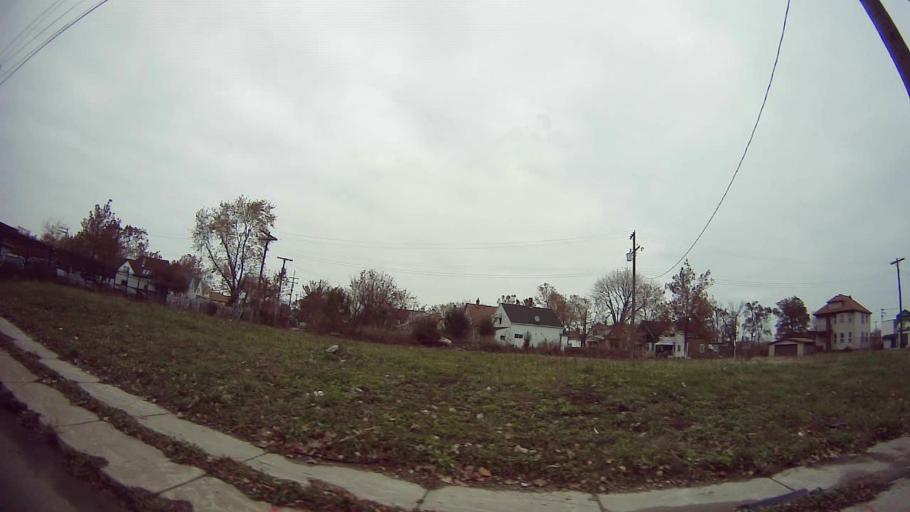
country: US
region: Michigan
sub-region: Wayne County
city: Hamtramck
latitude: 42.3873
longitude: -83.0405
